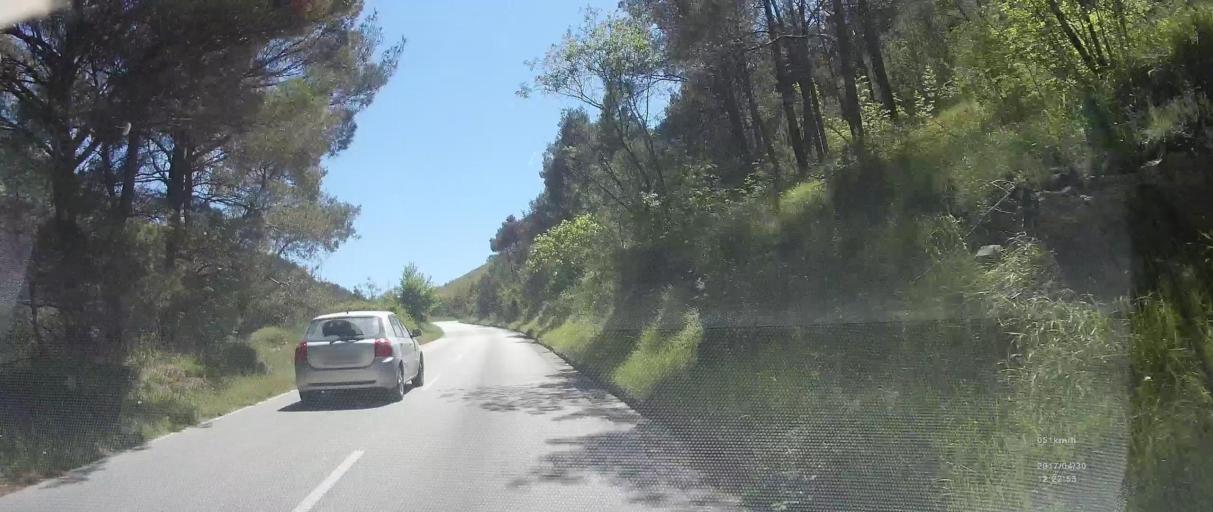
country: HR
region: Splitsko-Dalmatinska
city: Zrnovnica
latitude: 43.5188
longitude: 16.5739
